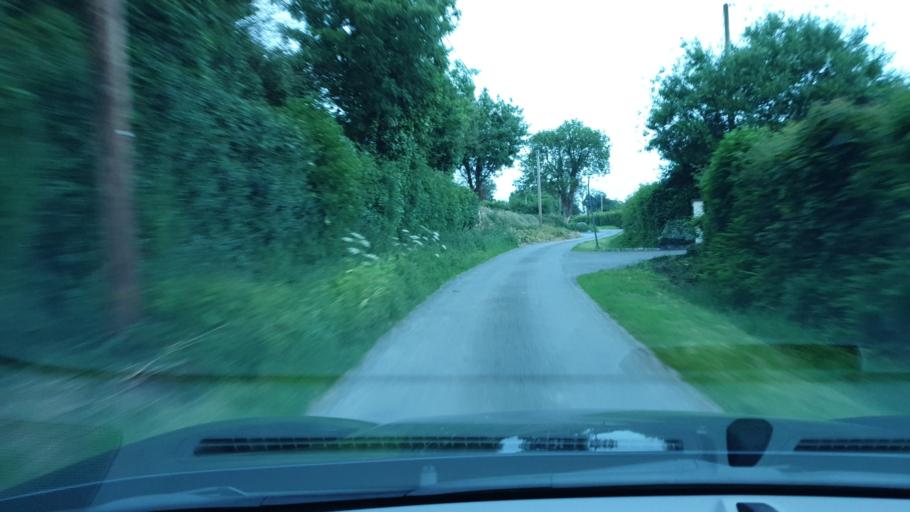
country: IE
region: Leinster
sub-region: An Mhi
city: Ashbourne
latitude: 53.5890
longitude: -6.3689
